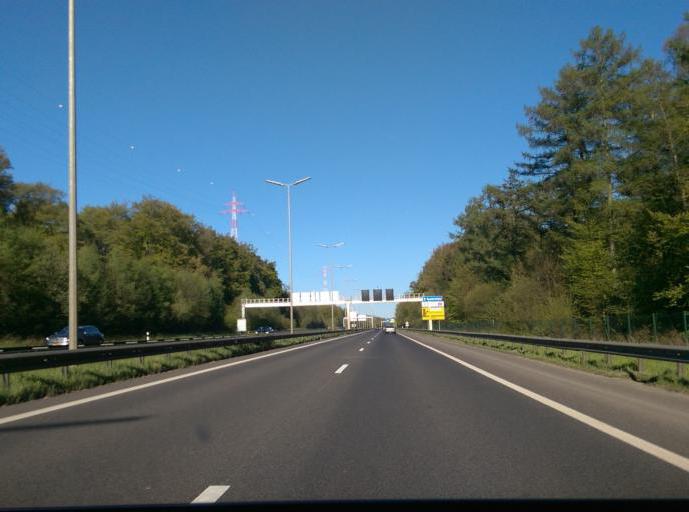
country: LU
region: Luxembourg
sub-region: Canton de Luxembourg
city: Sandweiler
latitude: 49.6419
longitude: 6.2016
